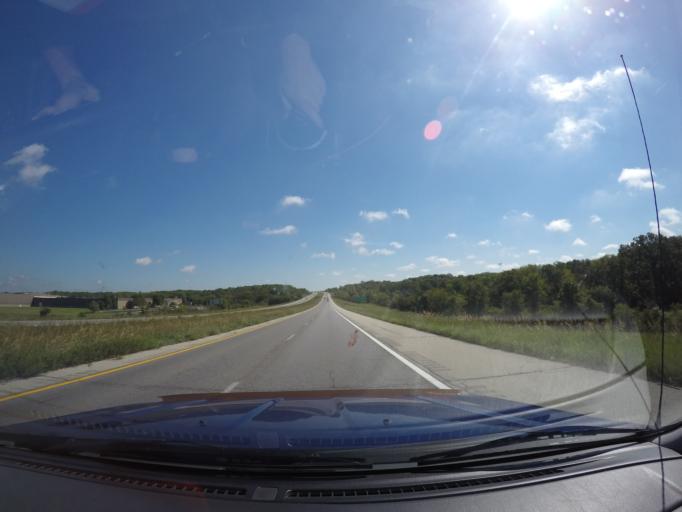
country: US
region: Kansas
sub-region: Johnson County
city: De Soto
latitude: 38.9603
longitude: -94.9755
